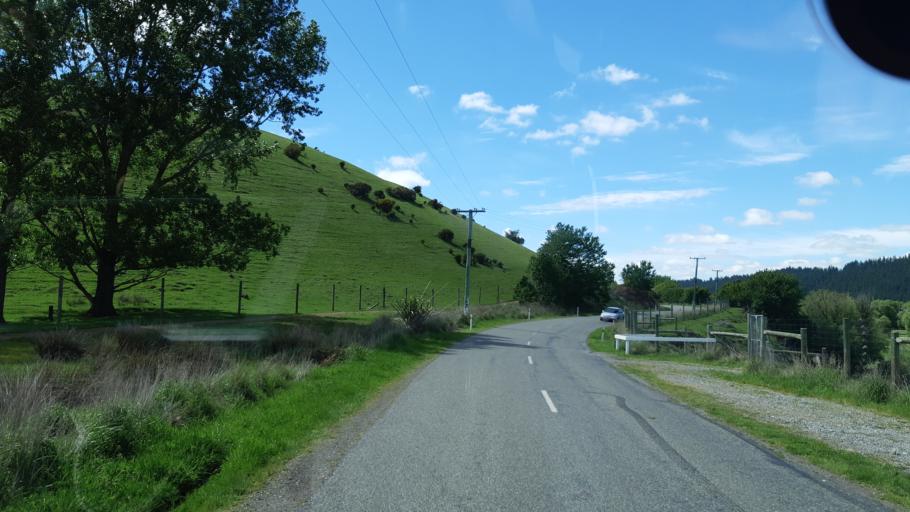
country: NZ
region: Canterbury
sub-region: Selwyn District
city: Darfield
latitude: -43.4782
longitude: 171.9177
